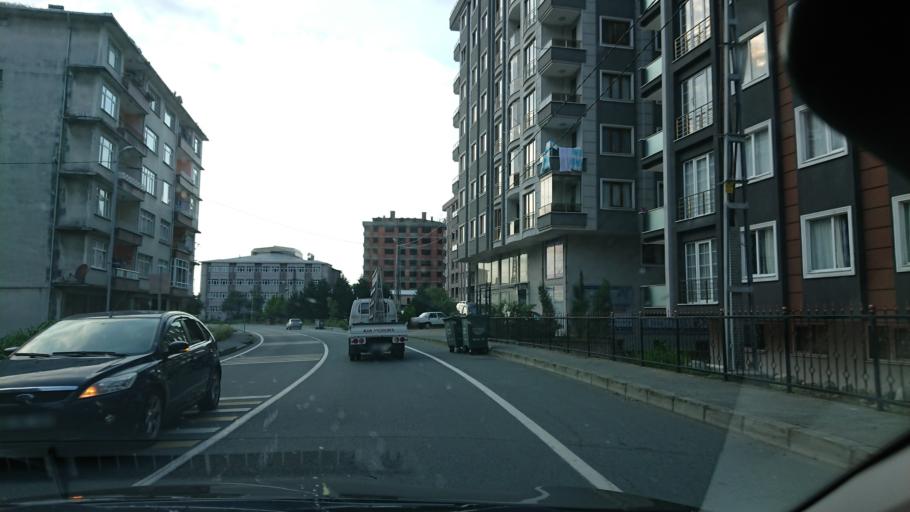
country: TR
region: Rize
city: Cayeli
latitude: 41.0812
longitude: 40.7124
